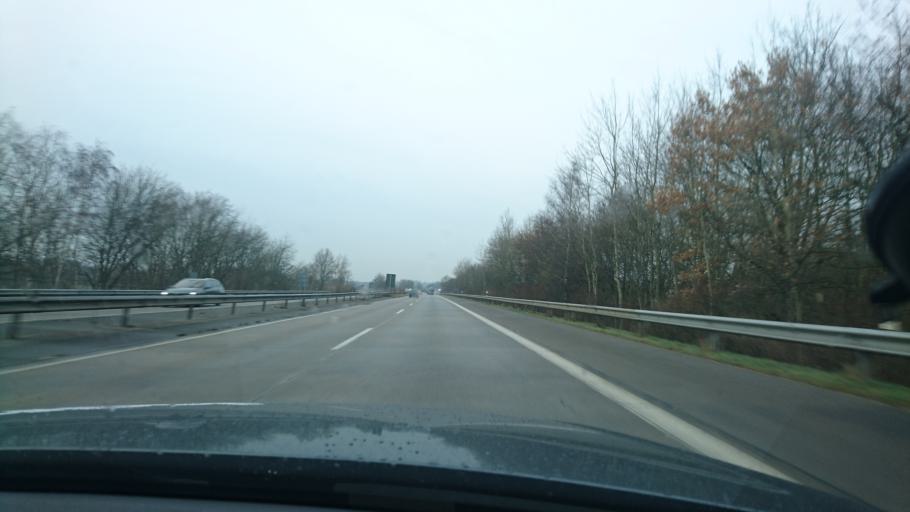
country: DE
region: Schleswig-Holstein
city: Ratekau
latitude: 53.9595
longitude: 10.7427
